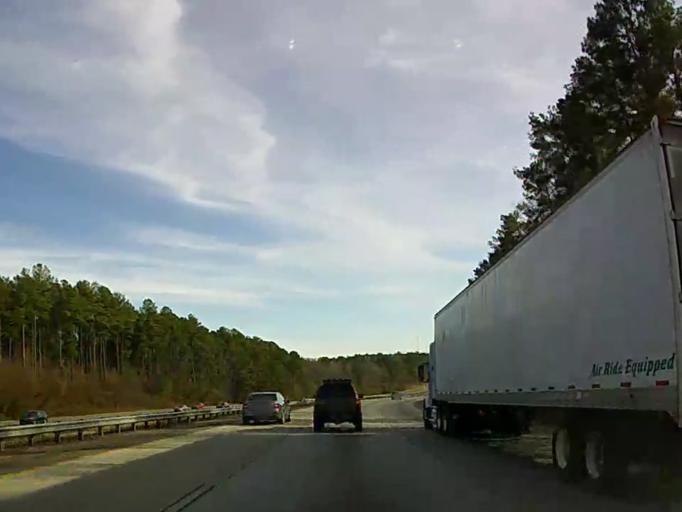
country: US
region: Georgia
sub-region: Monroe County
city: Forsyth
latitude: 32.9834
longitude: -83.8336
